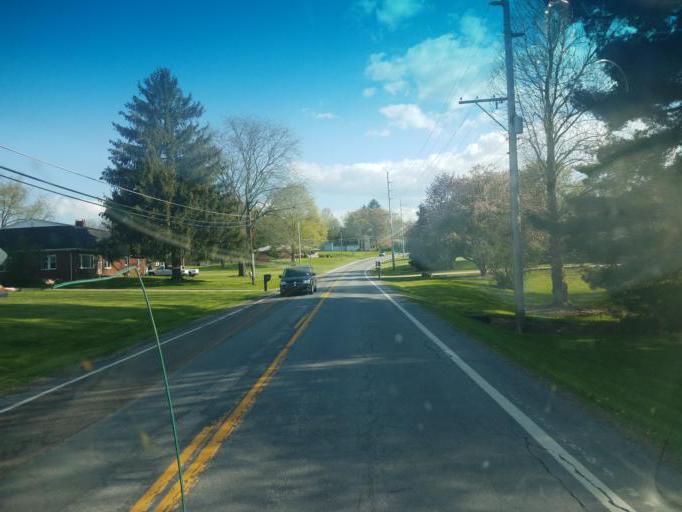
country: US
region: Ohio
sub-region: Wayne County
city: Shreve
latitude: 40.7176
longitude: -81.9439
